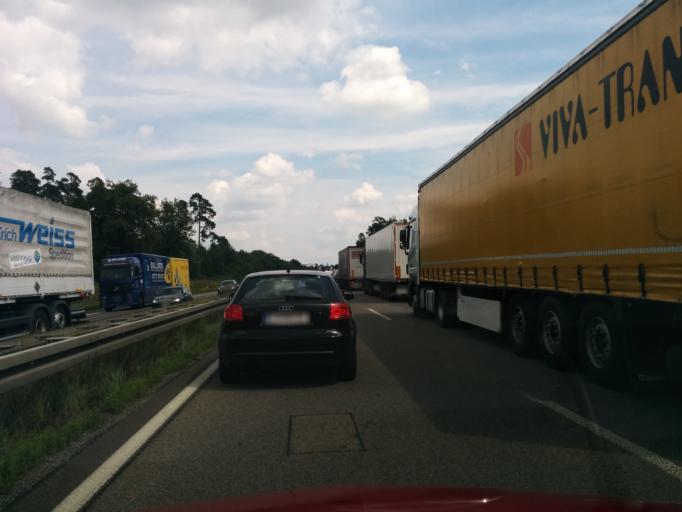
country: DE
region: Hesse
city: Romrod
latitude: 50.7120
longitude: 9.1684
